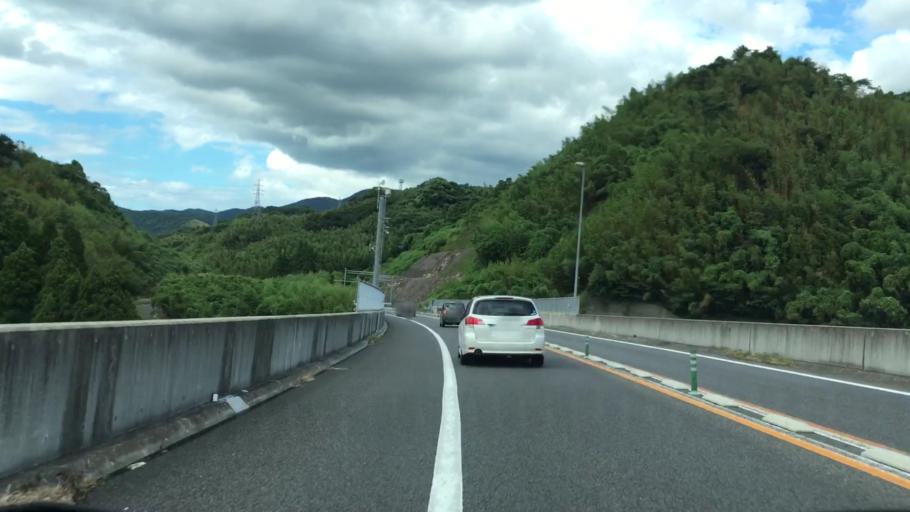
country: JP
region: Saga Prefecture
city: Karatsu
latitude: 33.4299
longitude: 130.0476
